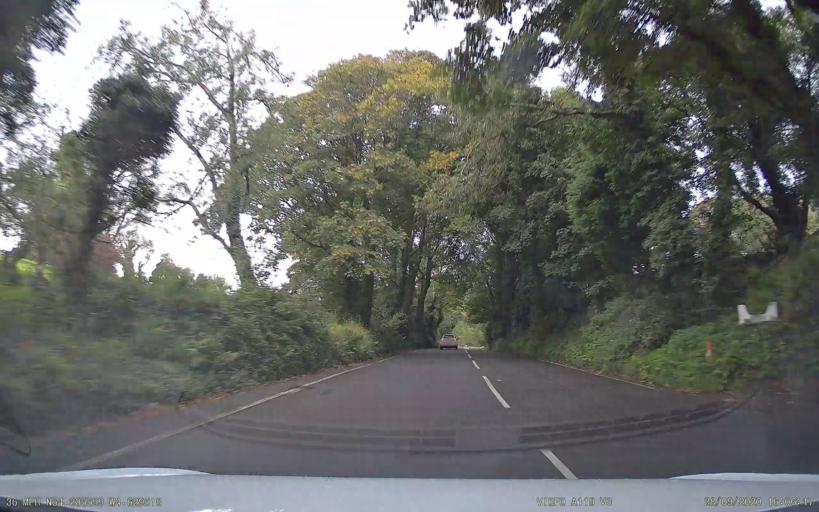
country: IM
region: Castletown
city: Castletown
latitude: 54.2056
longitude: -4.6300
